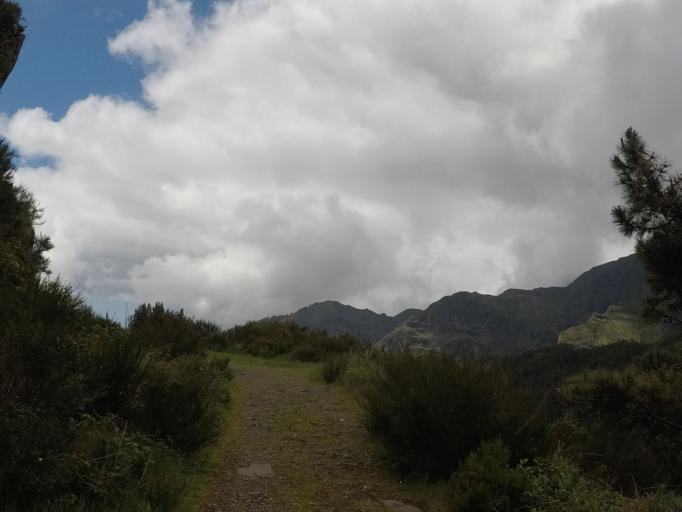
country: PT
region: Madeira
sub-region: Sao Vicente
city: Sao Vicente
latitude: 32.7493
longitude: -17.0179
